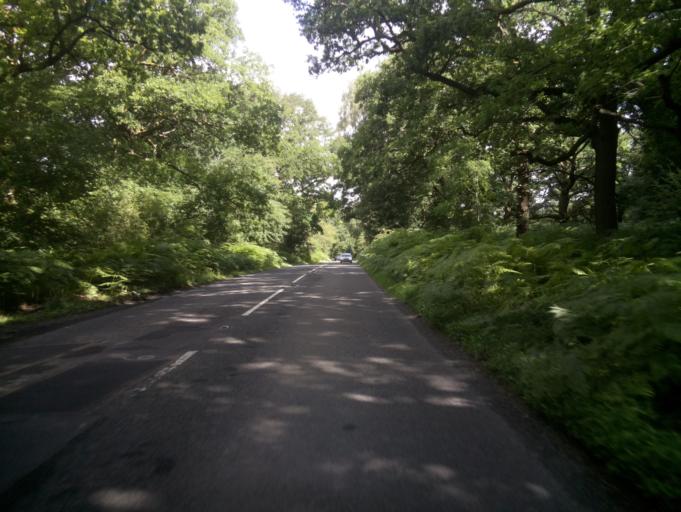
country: GB
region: England
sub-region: Gloucestershire
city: Bream
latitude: 51.7624
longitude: -2.5718
